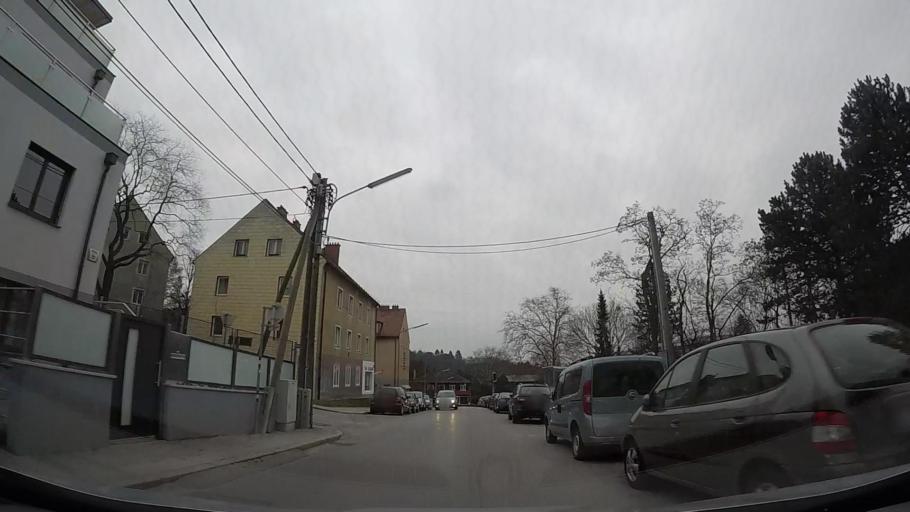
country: AT
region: Lower Austria
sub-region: Politischer Bezirk Wien-Umgebung
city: Purkersdorf
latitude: 48.2075
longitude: 16.2514
